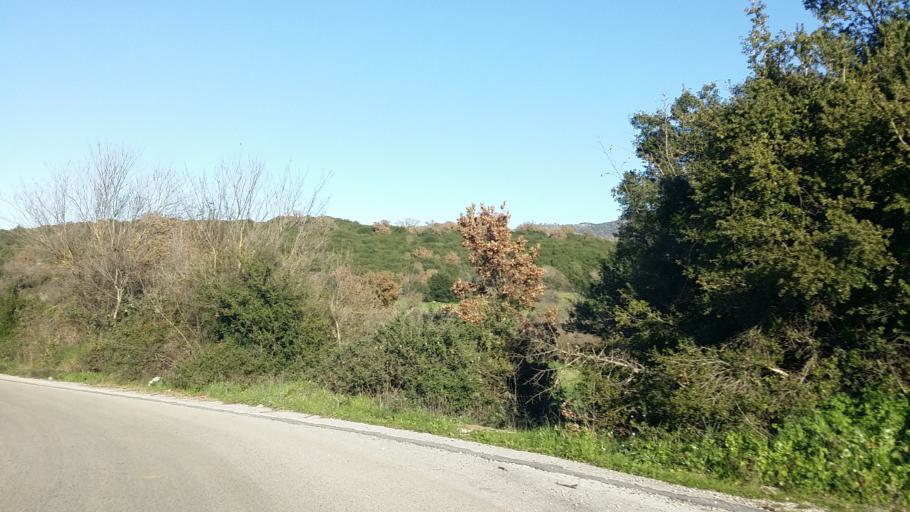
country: GR
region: West Greece
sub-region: Nomos Aitolias kai Akarnanias
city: Fitiai
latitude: 38.6334
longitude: 21.1609
